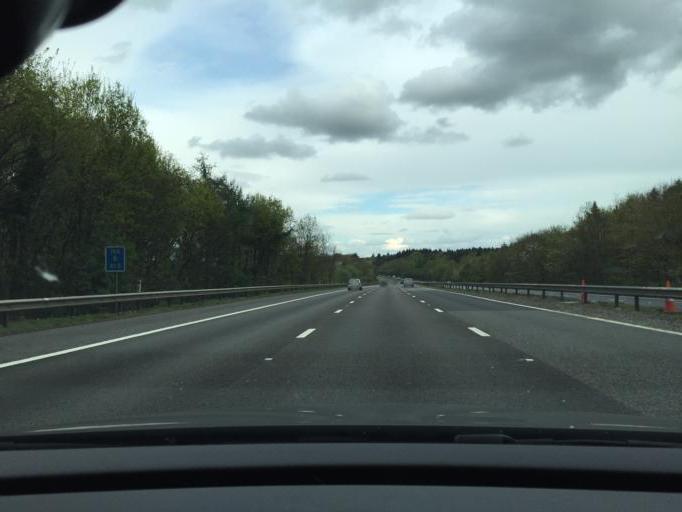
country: GB
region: England
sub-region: West Berkshire
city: Basildon
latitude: 51.4605
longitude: -1.1710
